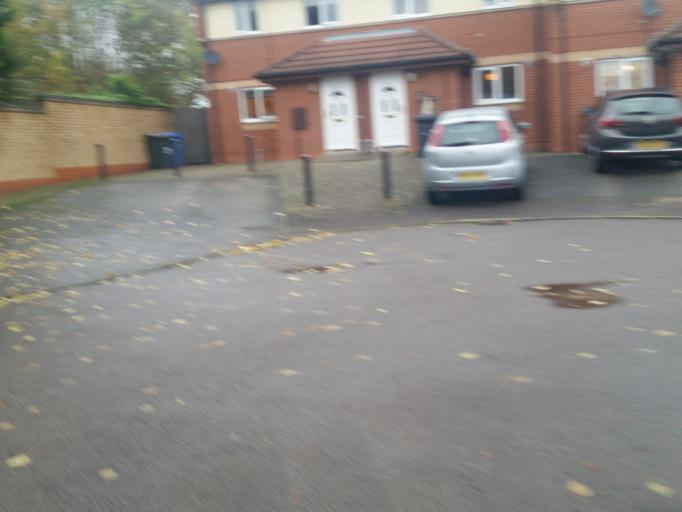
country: GB
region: England
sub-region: Derbyshire
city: Borrowash
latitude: 52.8957
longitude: -1.4165
